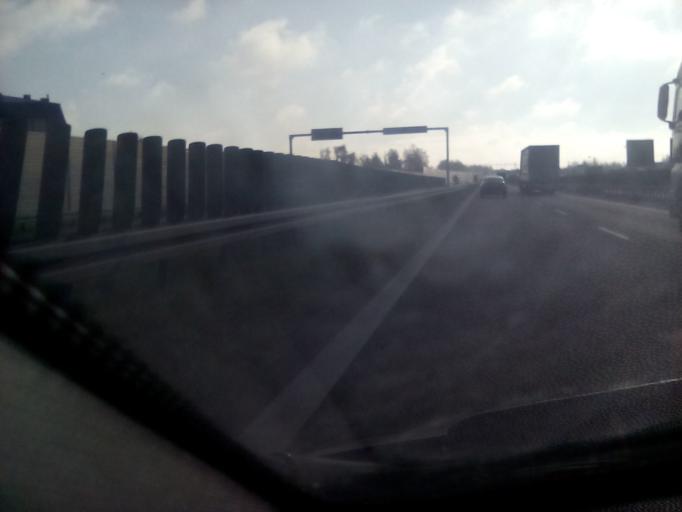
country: PL
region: Masovian Voivodeship
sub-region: Powiat grojecki
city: Grojec
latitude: 51.8589
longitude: 20.8578
